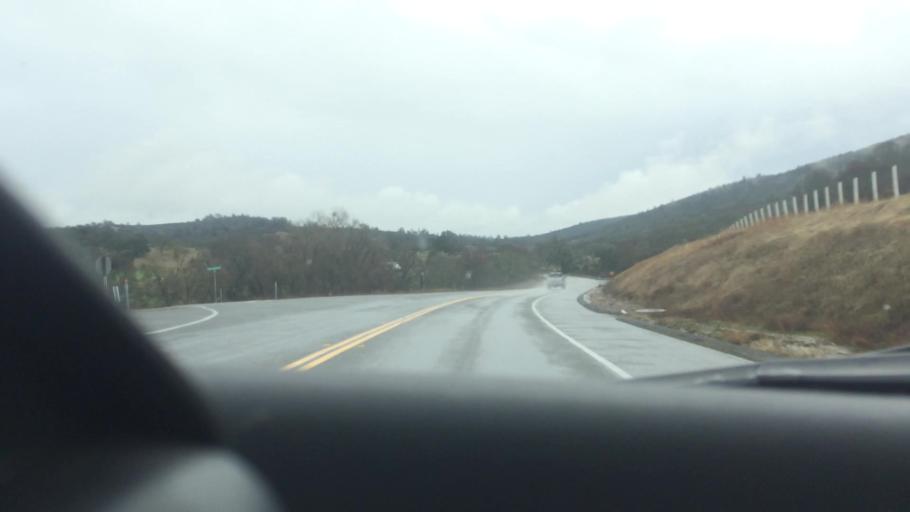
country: US
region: California
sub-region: El Dorado County
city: Cameron Park
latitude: 38.6032
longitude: -121.0250
